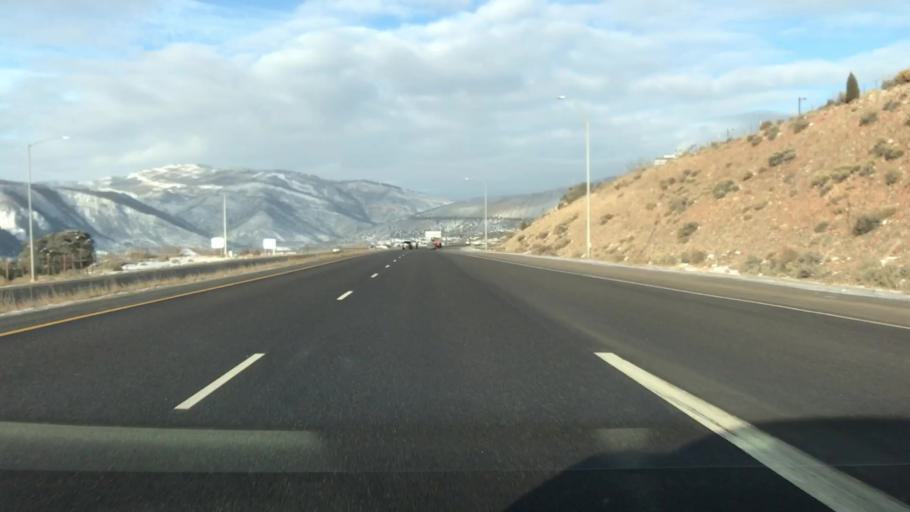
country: US
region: Colorado
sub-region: Eagle County
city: Edwards
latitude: 39.6507
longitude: -106.5910
